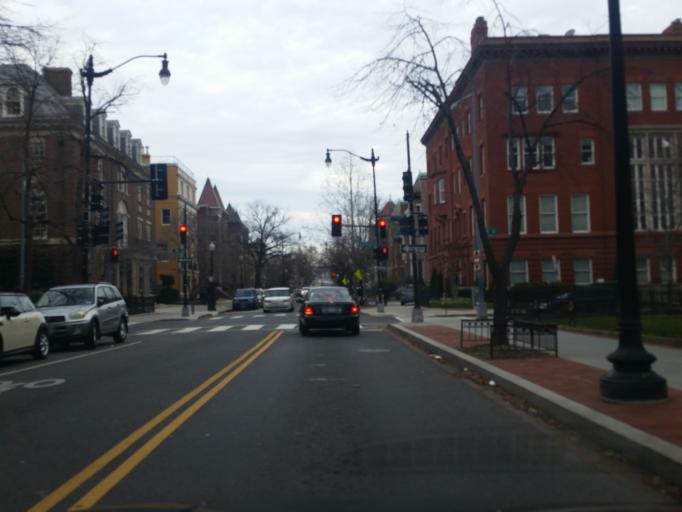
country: US
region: Washington, D.C.
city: Washington, D.C.
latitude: 38.9123
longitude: -77.0416
